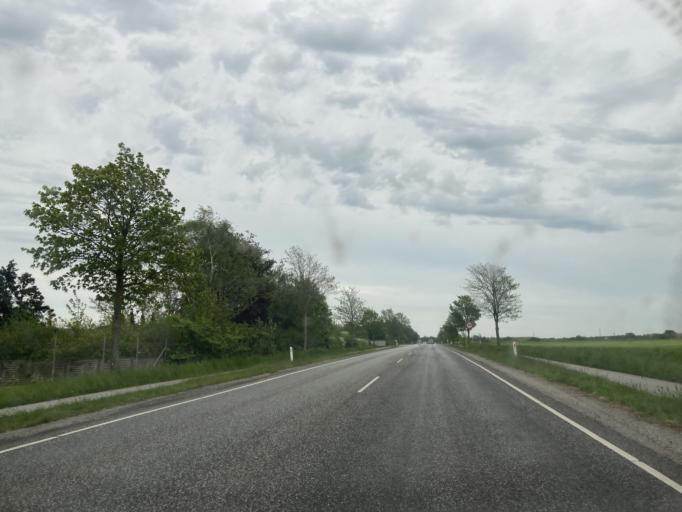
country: DK
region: Zealand
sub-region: Roskilde Kommune
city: Svogerslev
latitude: 55.6319
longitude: 12.0061
